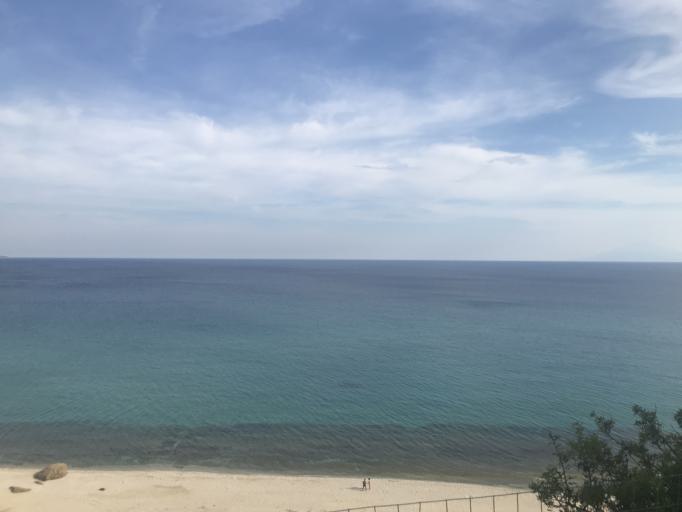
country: GR
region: East Macedonia and Thrace
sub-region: Nomos Kavalas
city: Limenaria
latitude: 40.6249
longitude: 24.5521
